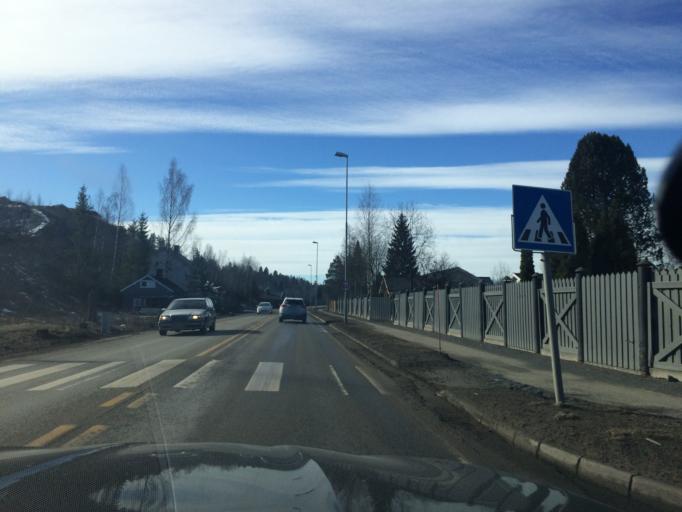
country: NO
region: Hedmark
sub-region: Elverum
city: Elverum
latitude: 60.8915
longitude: 11.5742
